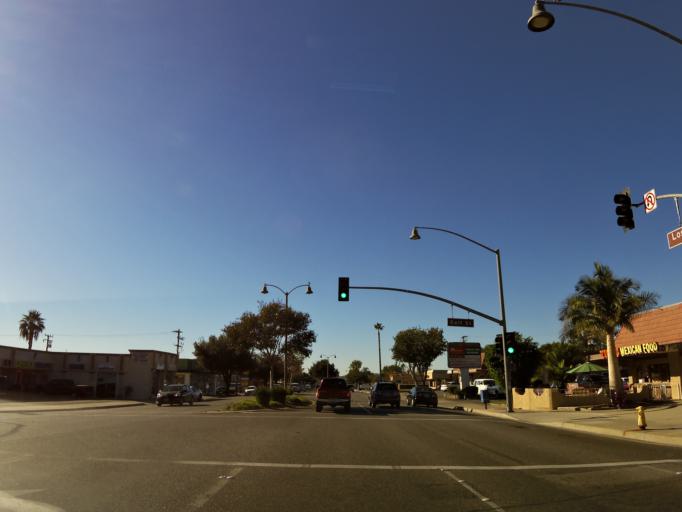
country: US
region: California
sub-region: Ventura County
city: Simi Valley
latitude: 34.2717
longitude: -118.7657
